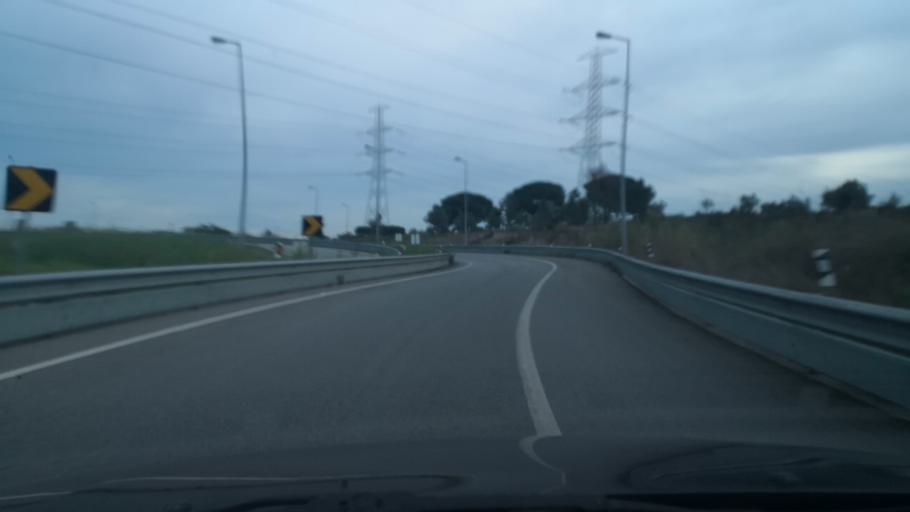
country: PT
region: Setubal
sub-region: Setubal
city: Setubal
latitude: 38.5372
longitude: -8.8441
